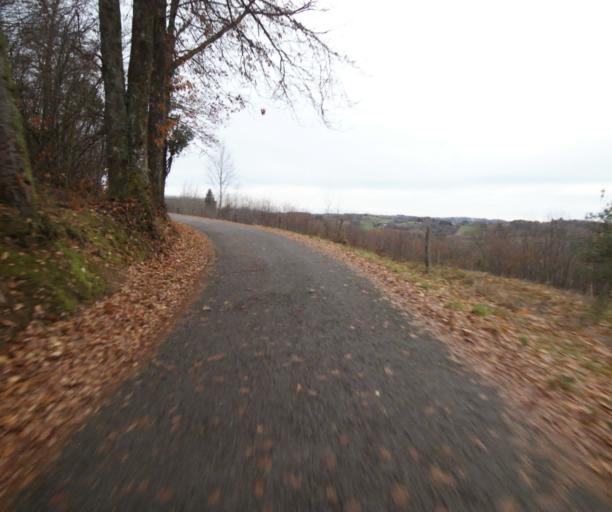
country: FR
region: Limousin
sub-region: Departement de la Correze
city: Chameyrat
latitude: 45.2340
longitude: 1.6541
